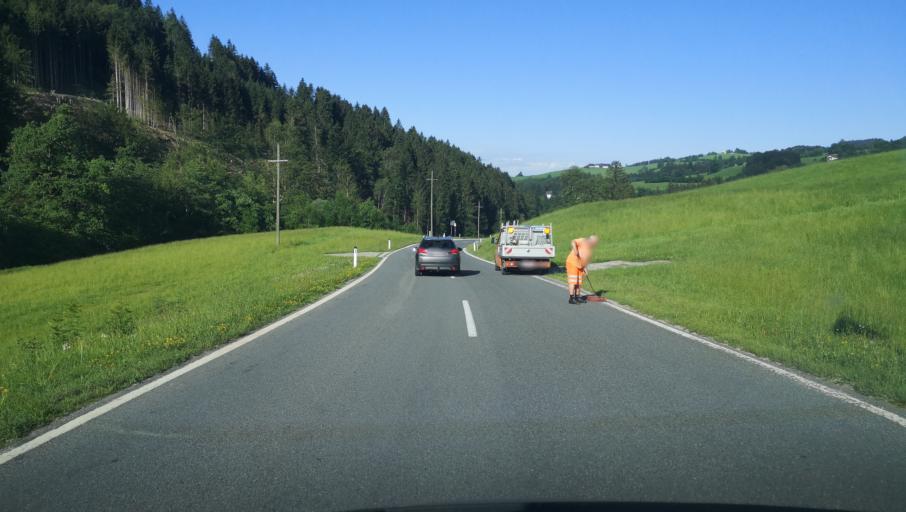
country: AT
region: Lower Austria
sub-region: Politischer Bezirk Scheibbs
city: Randegg
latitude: 47.9662
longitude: 14.9486
